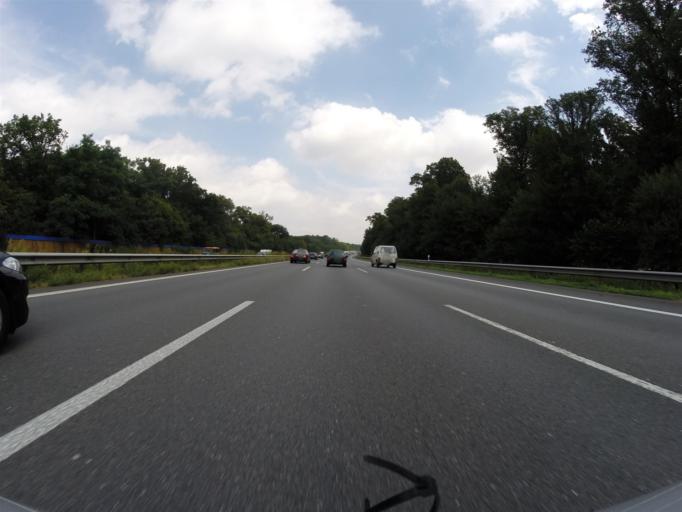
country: DE
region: North Rhine-Westphalia
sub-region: Regierungsbezirk Detmold
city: Leopoldshohe
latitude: 52.0342
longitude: 8.6404
